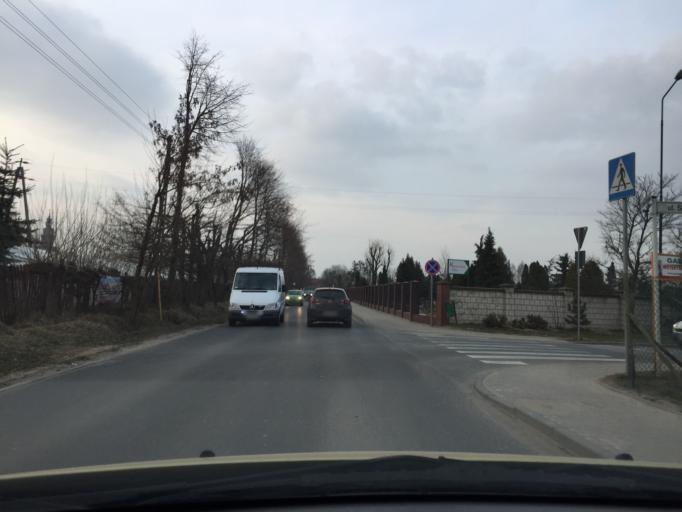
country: PL
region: Greater Poland Voivodeship
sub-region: Powiat poznanski
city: Plewiska
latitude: 52.3893
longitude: 16.7954
